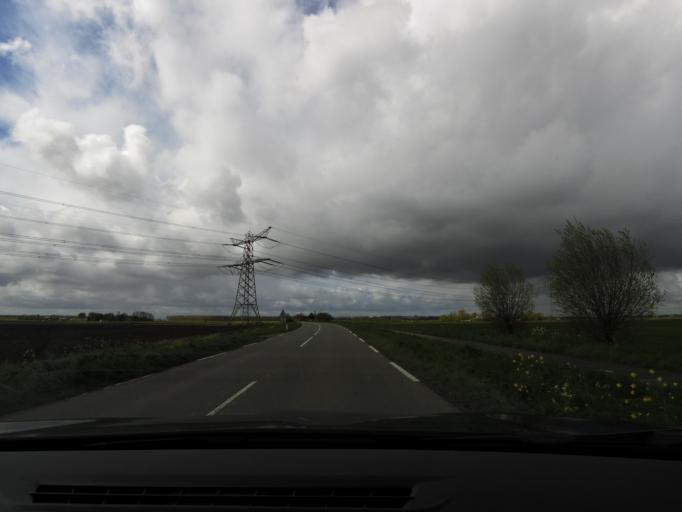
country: NL
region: South Holland
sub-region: Gemeente Spijkenisse
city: Spijkenisse
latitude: 51.8228
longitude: 4.3201
